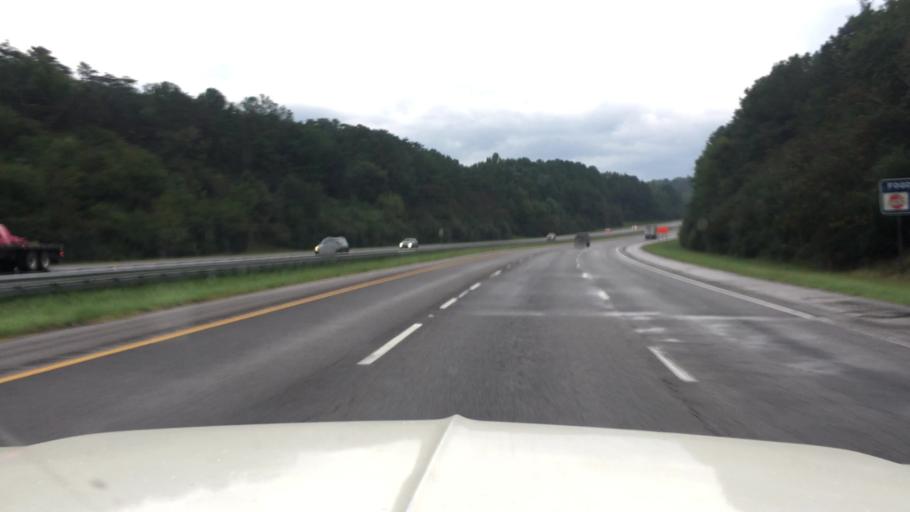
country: US
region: Alabama
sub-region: Jefferson County
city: Gardendale
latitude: 33.6825
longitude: -86.8281
